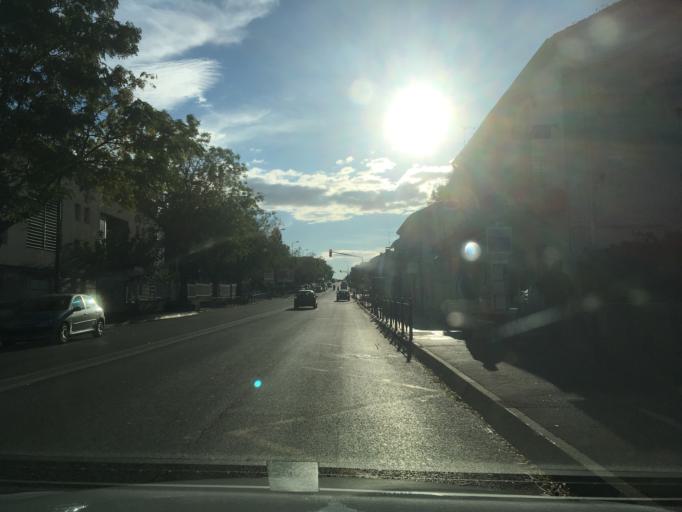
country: FR
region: Languedoc-Roussillon
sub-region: Departement de l'Herault
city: Montpellier
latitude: 43.5961
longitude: 3.8627
